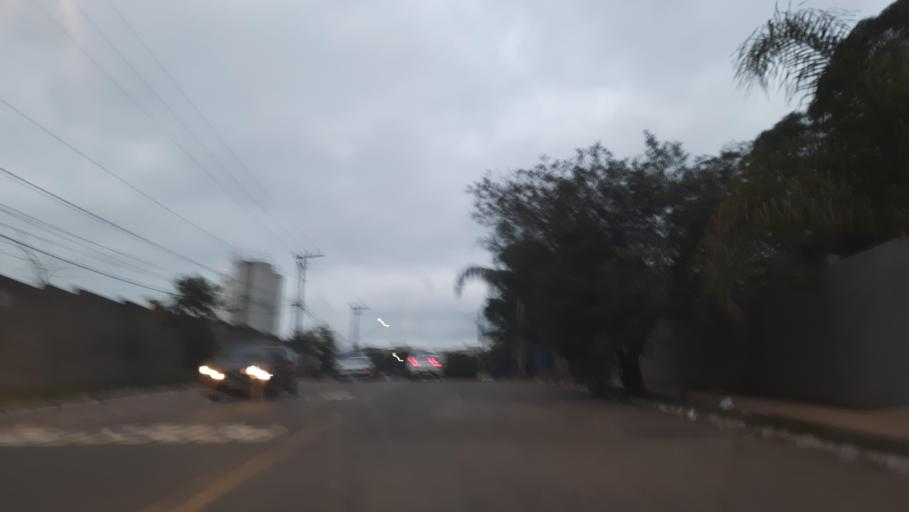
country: BR
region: Sao Paulo
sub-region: Caieiras
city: Caieiras
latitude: -23.4447
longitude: -46.7261
